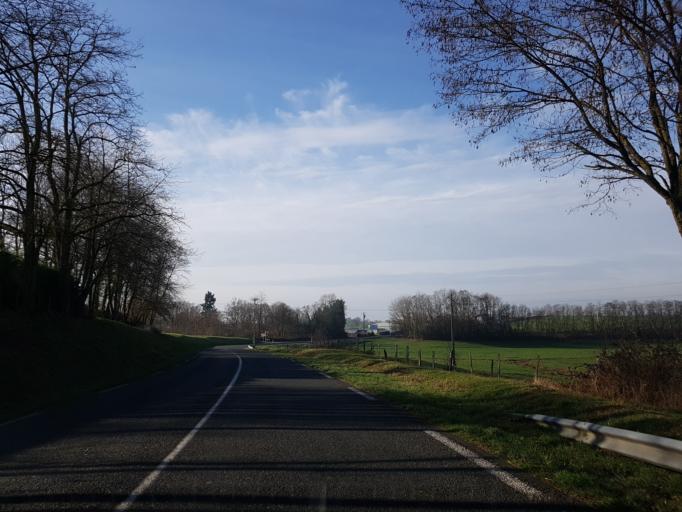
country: FR
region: Bourgogne
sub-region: Departement de Saone-et-Loire
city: La Motte-Saint-Jean
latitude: 46.5936
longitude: 3.9323
